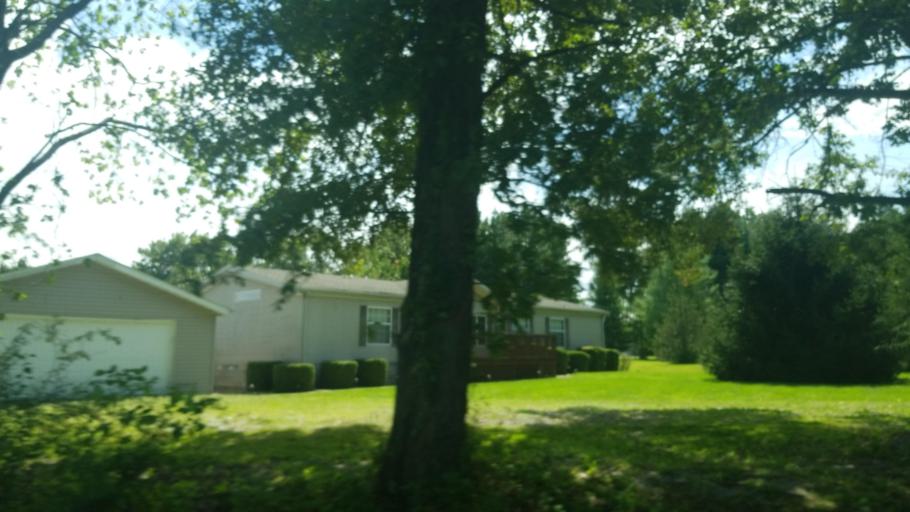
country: US
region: Illinois
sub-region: Saline County
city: Carrier Mills
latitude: 37.7915
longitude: -88.7621
